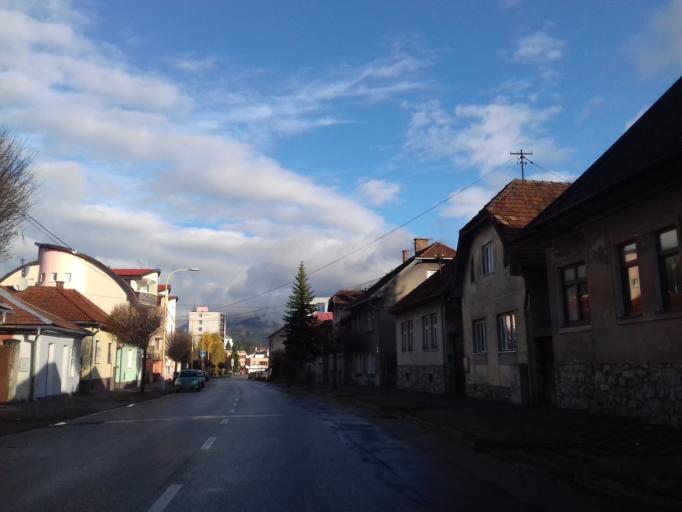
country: SK
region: Zilinsky
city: Ruzomberok
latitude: 49.0762
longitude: 19.3037
